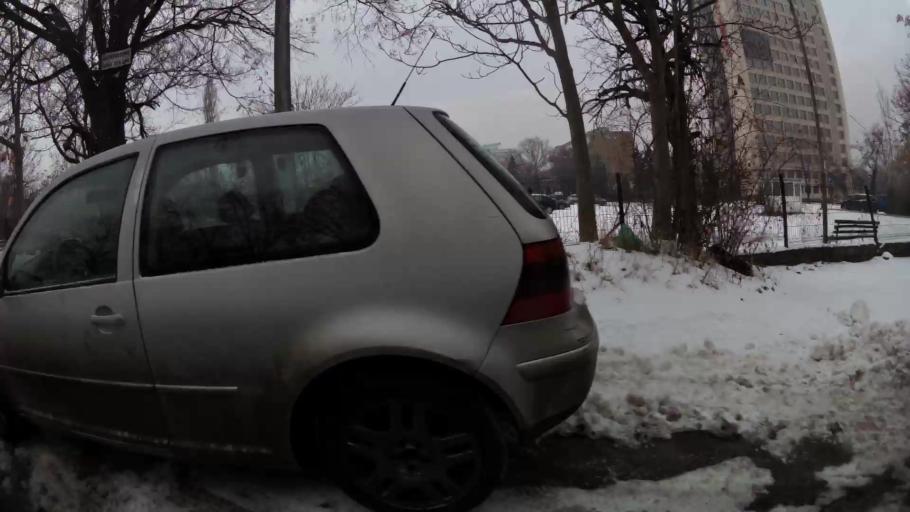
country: BG
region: Sofia-Capital
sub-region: Stolichna Obshtina
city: Sofia
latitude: 42.7164
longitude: 23.2970
